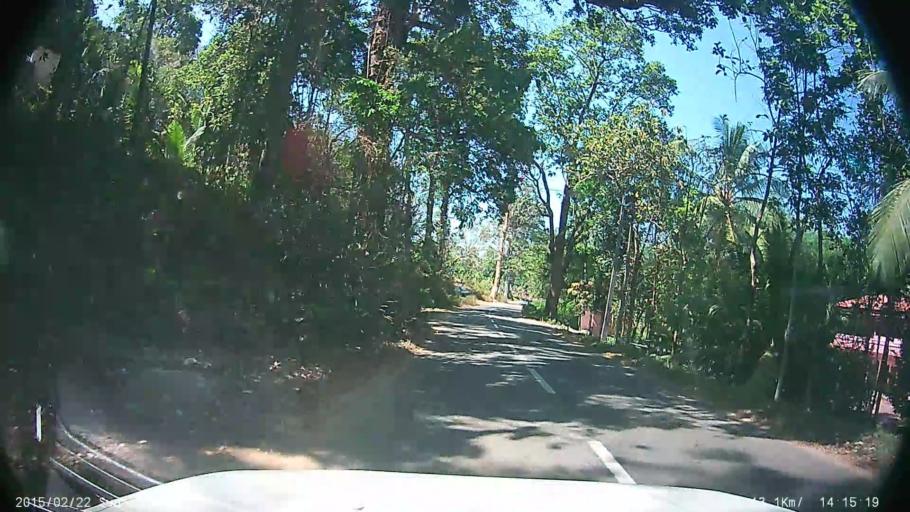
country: IN
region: Kerala
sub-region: Kottayam
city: Kottayam
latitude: 9.5487
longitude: 76.6841
